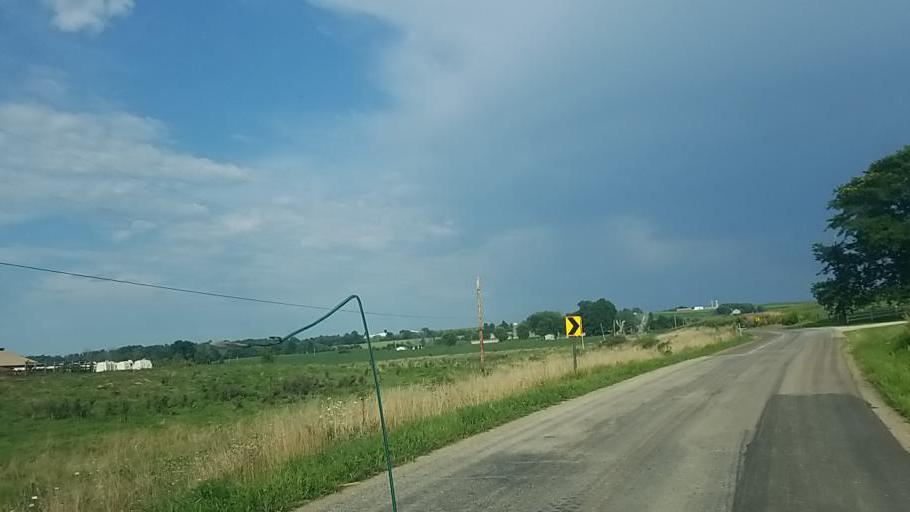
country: US
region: Ohio
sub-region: Wayne County
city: Smithville
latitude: 40.9161
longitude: -81.8858
